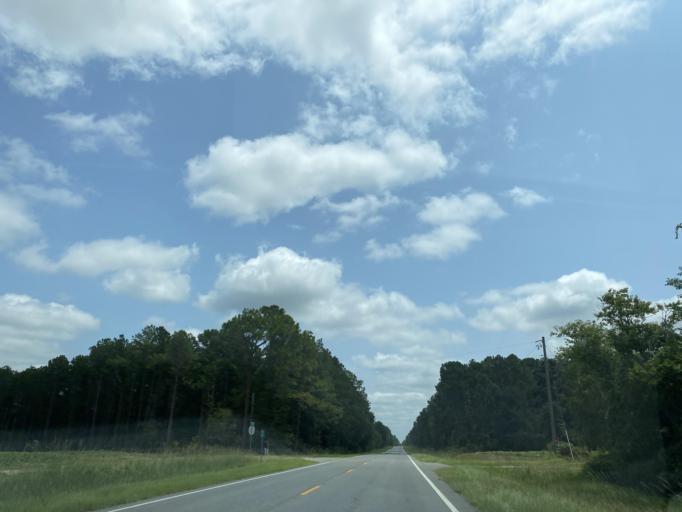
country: US
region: Georgia
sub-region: Bacon County
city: Alma
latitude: 31.7028
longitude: -82.5134
